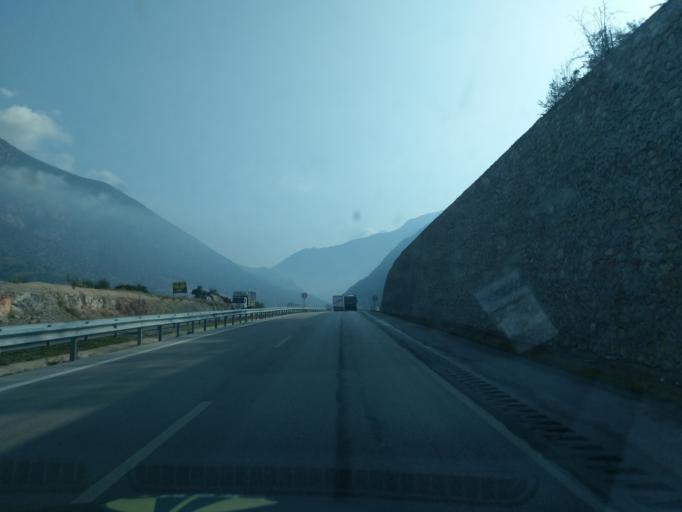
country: TR
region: Amasya
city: Akdag
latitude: 40.6917
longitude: 35.9204
